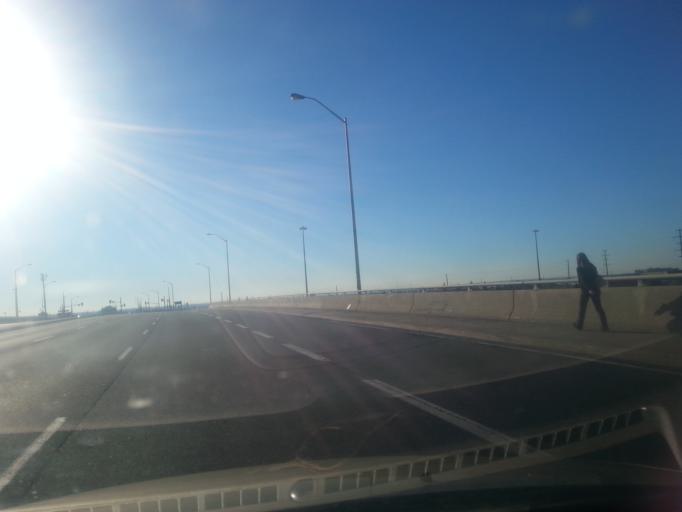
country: CA
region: Ontario
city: Concord
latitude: 43.7916
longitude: -79.5386
